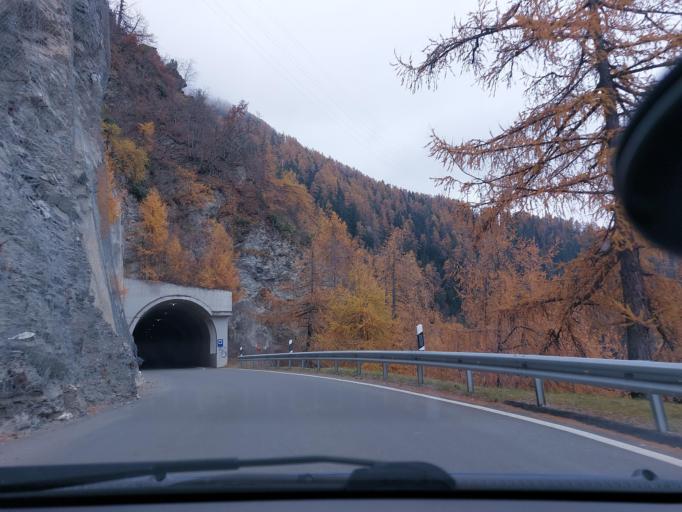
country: CH
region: Valais
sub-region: Martigny District
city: Riddes
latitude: 46.1729
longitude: 7.2495
